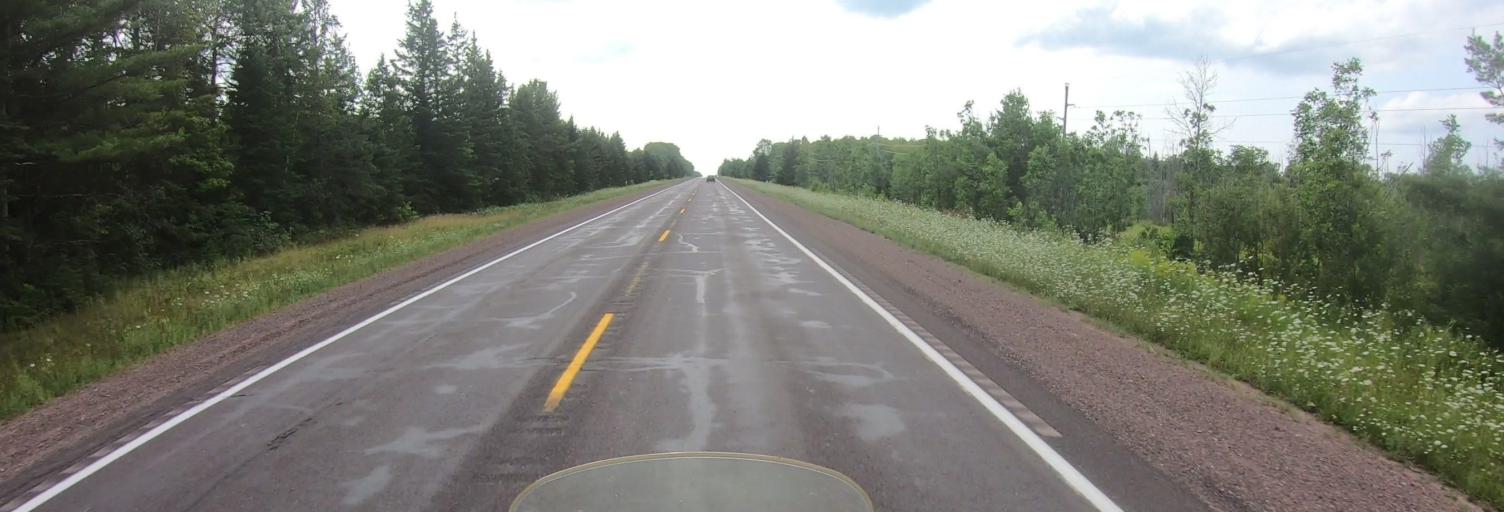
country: US
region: Michigan
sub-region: Gogebic County
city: Wakefield
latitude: 46.5607
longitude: -89.6846
